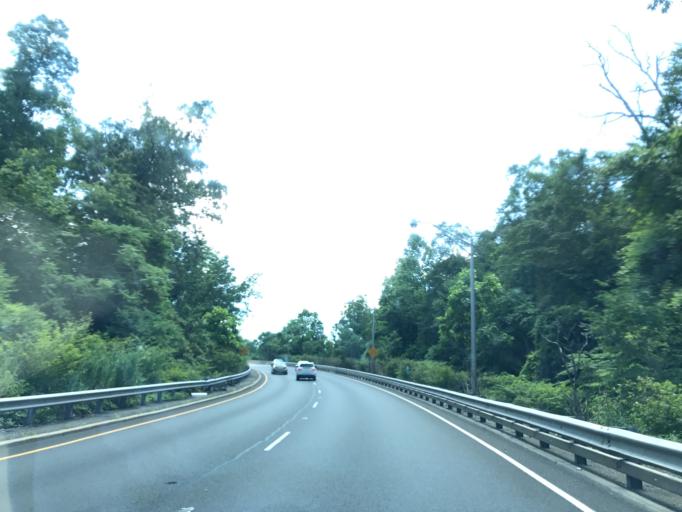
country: US
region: New Jersey
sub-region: Morris County
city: Morris Plains
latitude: 40.8122
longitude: -74.4484
